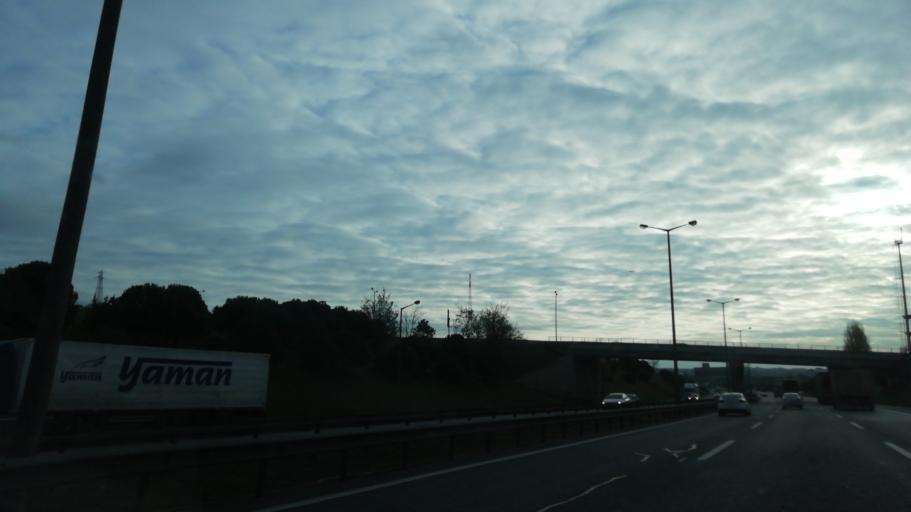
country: TR
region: Istanbul
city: Sultanbeyli
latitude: 40.9369
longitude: 29.3307
